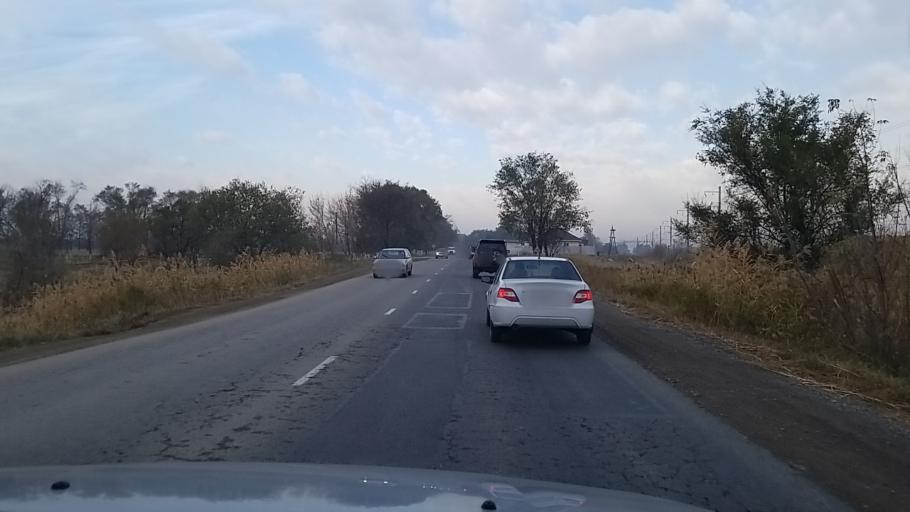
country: KZ
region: Almaty Oblysy
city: Burunday
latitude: 43.3587
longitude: 76.7706
